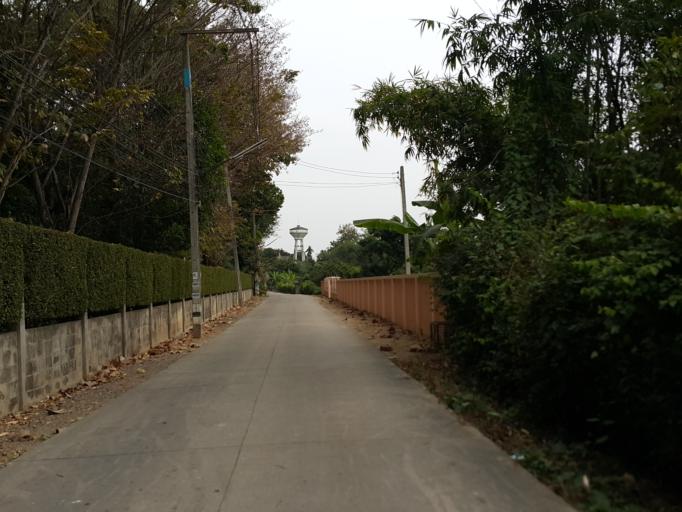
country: TH
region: Chiang Mai
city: Saraphi
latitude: 18.7391
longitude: 99.0195
